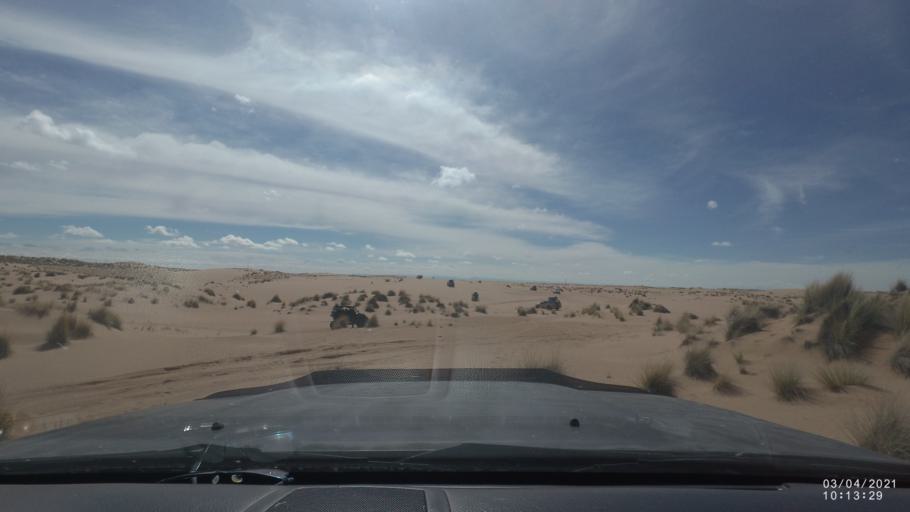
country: BO
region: Oruro
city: Poopo
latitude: -18.7047
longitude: -67.5276
